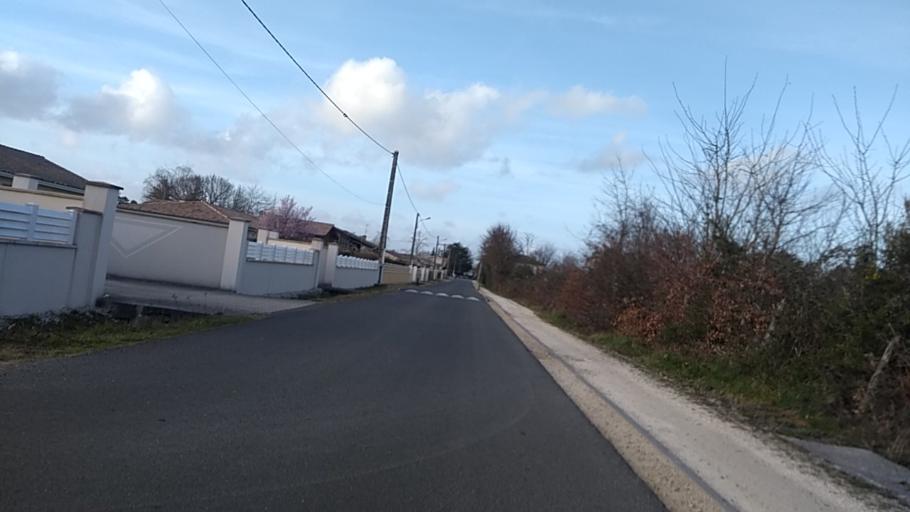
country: FR
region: Aquitaine
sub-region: Departement de la Gironde
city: Le Barp
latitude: 44.5990
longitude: -0.7684
